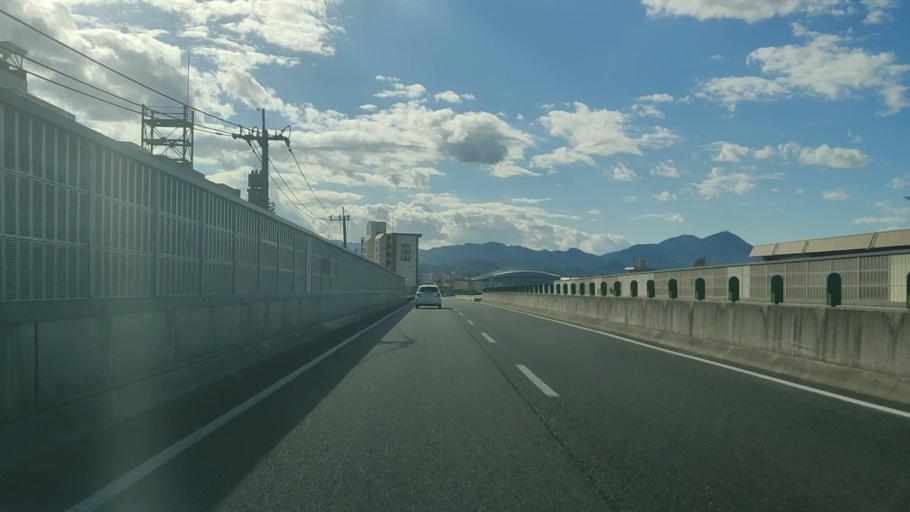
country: JP
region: Yamaguchi
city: Shimonoseki
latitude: 33.8813
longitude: 130.9042
